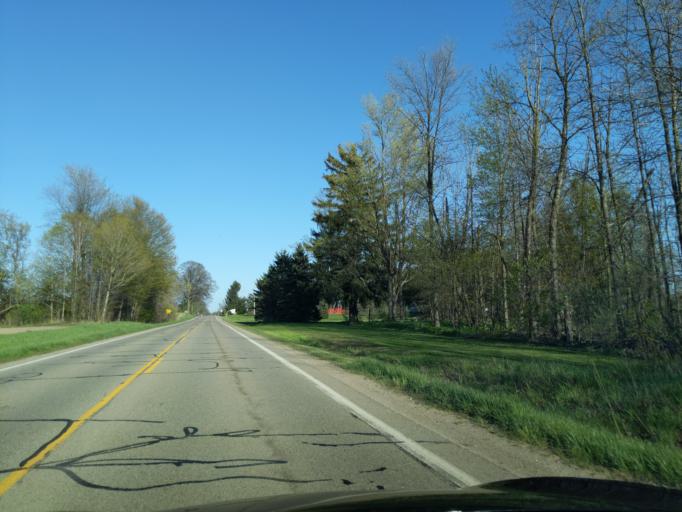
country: US
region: Michigan
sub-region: Ionia County
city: Portland
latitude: 42.8155
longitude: -84.8273
